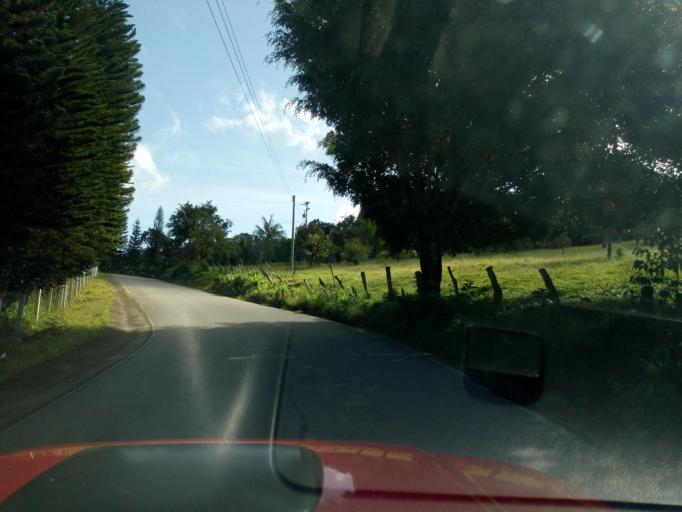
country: CO
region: Boyaca
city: Moniquira
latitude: 5.8806
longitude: -73.5463
